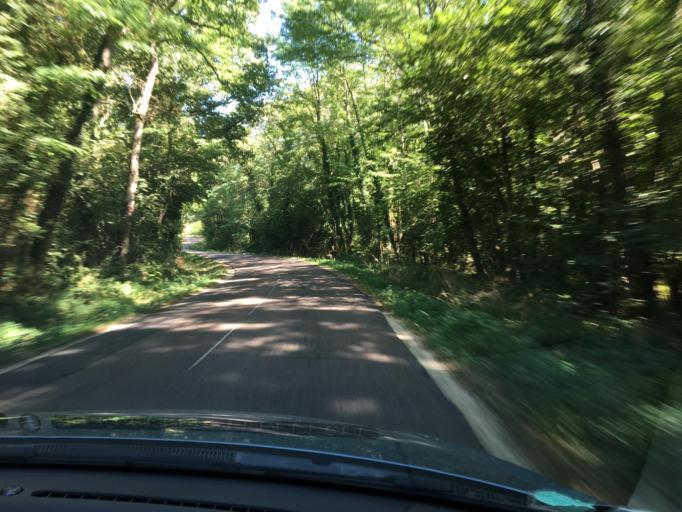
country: FR
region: Bourgogne
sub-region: Departement de l'Yonne
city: Appoigny
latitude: 47.8721
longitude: 3.4936
